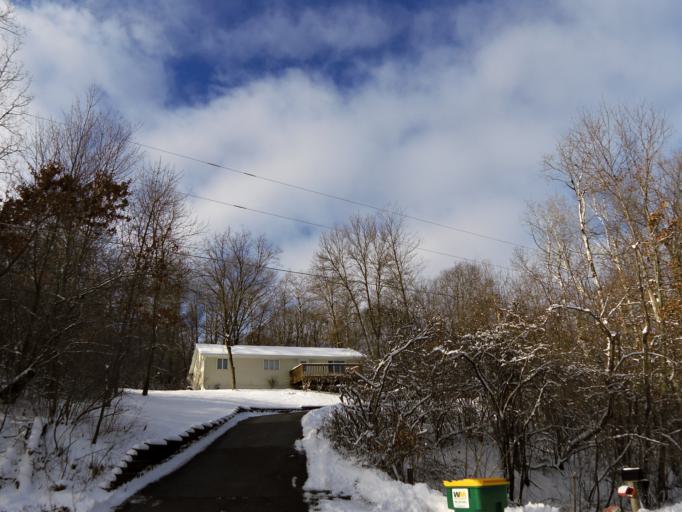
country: US
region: Minnesota
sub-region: Washington County
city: Lake Elmo
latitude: 44.9722
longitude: -92.8377
